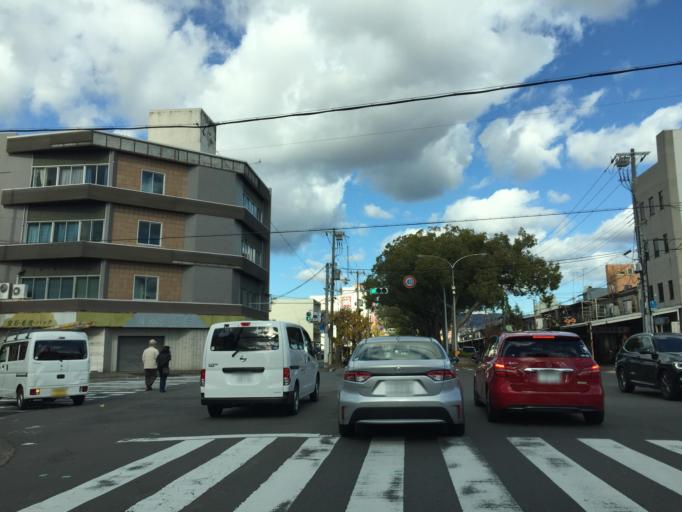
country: JP
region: Wakayama
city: Wakayama-shi
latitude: 34.2353
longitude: 135.1770
